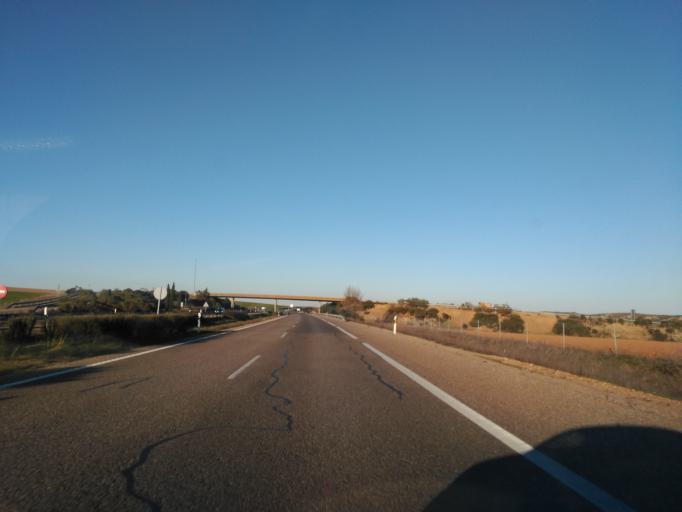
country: ES
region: Castille and Leon
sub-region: Provincia de Zamora
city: Canizal
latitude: 41.1721
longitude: -5.3759
